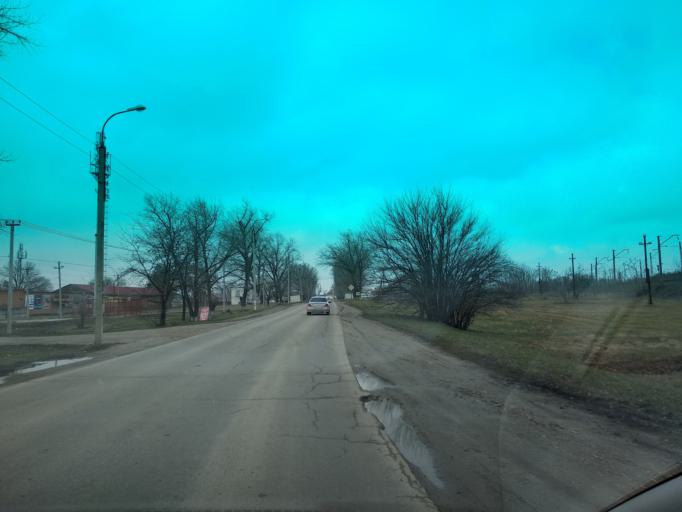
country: RU
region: Krasnodarskiy
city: Parkovyy
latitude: 45.8368
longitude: 40.1286
